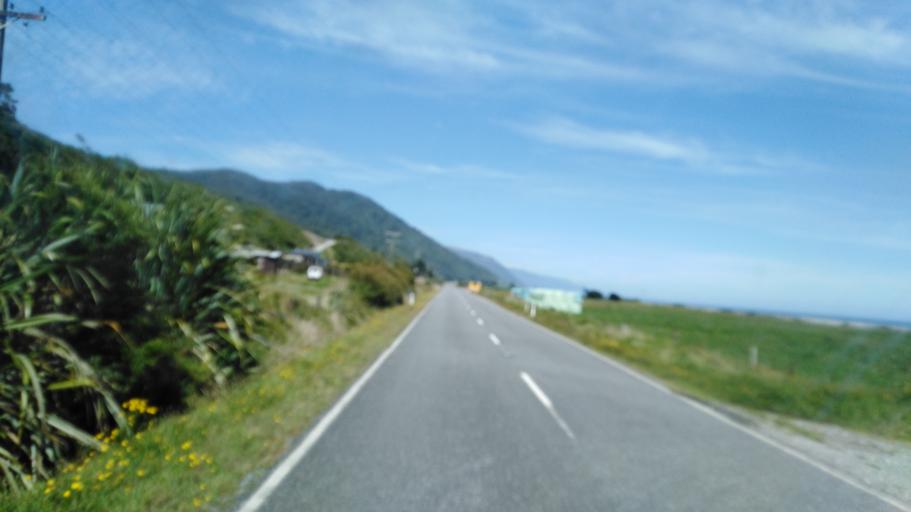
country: NZ
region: West Coast
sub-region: Buller District
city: Westport
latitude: -41.5443
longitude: 171.9263
